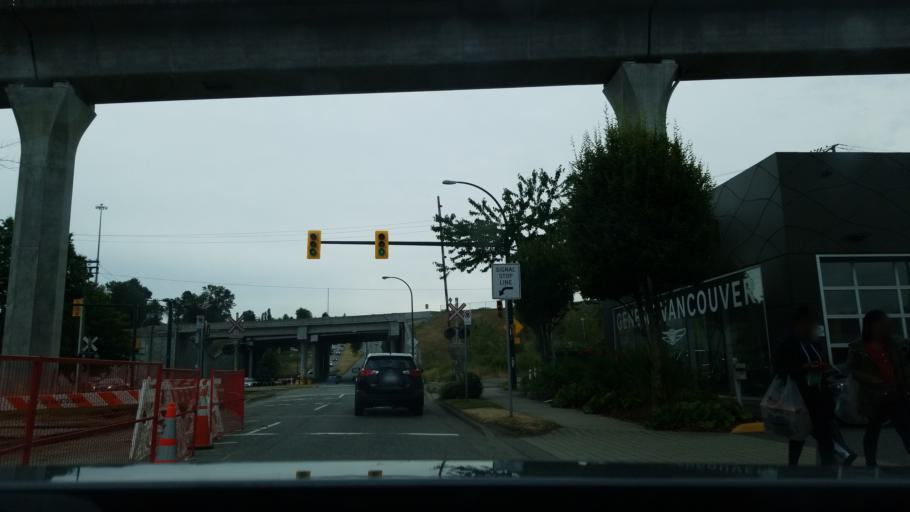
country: CA
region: British Columbia
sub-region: Fraser Valley Regional District
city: North Vancouver
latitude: 49.2627
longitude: -123.0238
